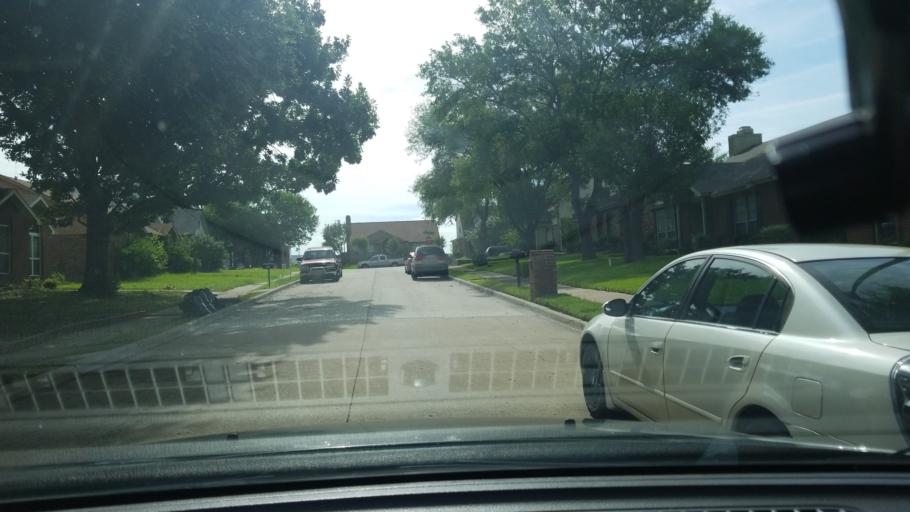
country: US
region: Texas
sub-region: Dallas County
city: Balch Springs
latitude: 32.7745
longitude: -96.6614
